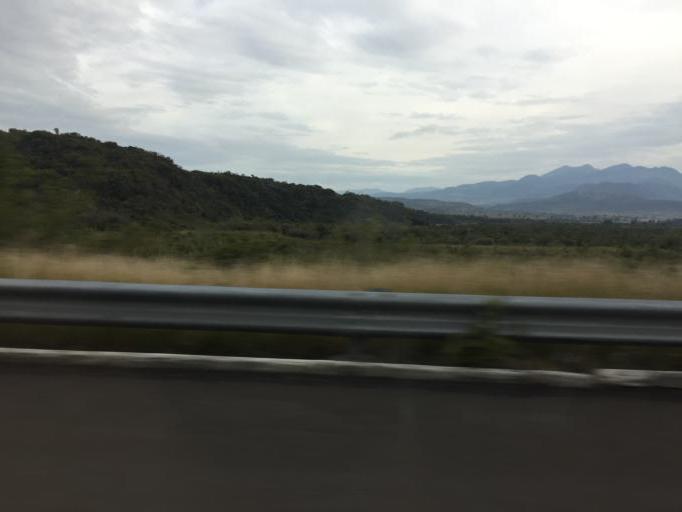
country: MX
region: Mexico
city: Huaniqueo de Morales
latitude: 19.8869
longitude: -101.4641
